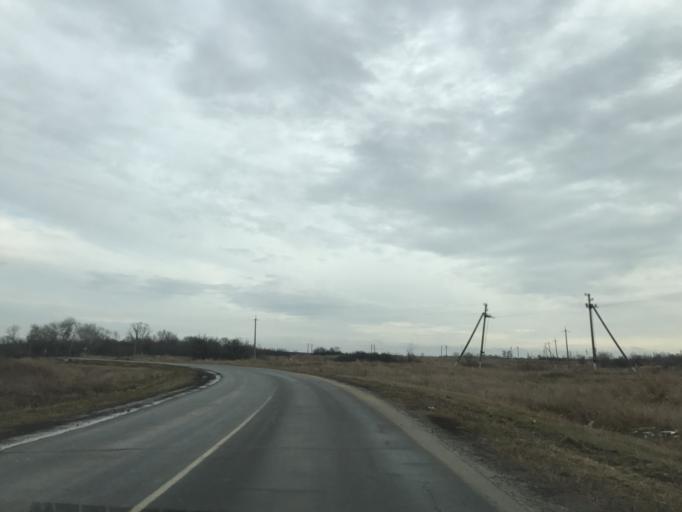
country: RU
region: Rostov
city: Glubokiy
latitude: 48.4842
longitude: 40.3130
